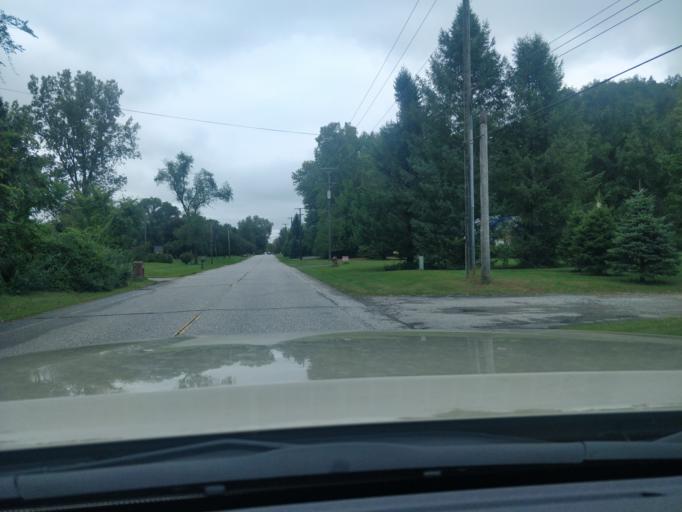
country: US
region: Michigan
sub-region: Wayne County
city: Romulus
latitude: 42.1827
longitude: -83.4178
